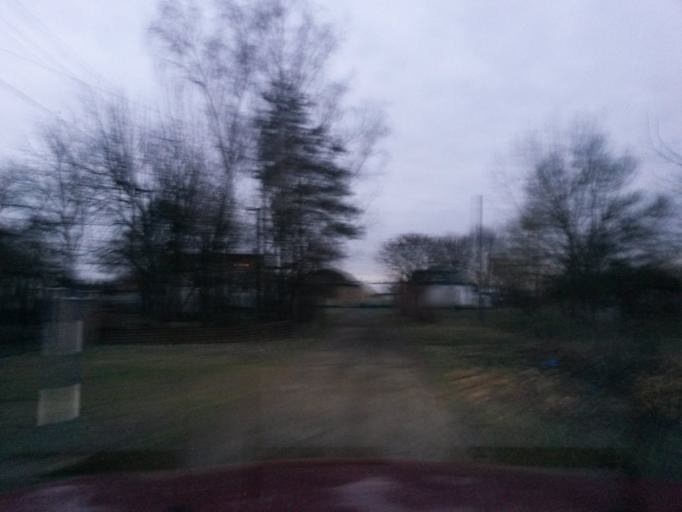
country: SK
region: Kosicky
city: Michalovce
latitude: 48.6666
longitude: 22.0289
